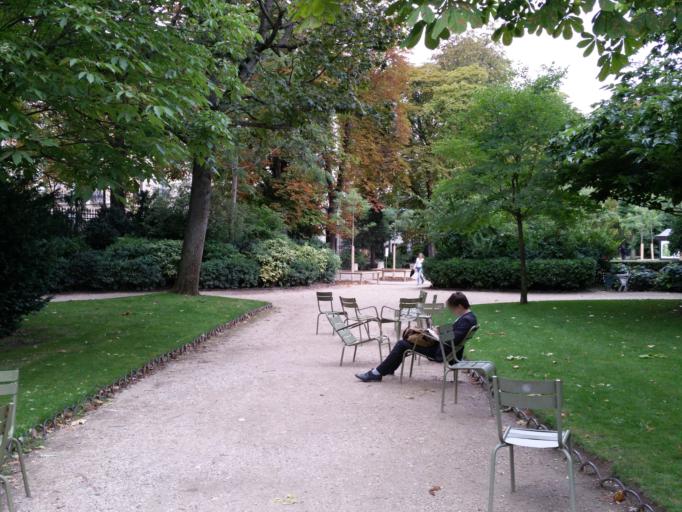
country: FR
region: Ile-de-France
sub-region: Paris
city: Paris
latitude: 48.8466
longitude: 2.3330
